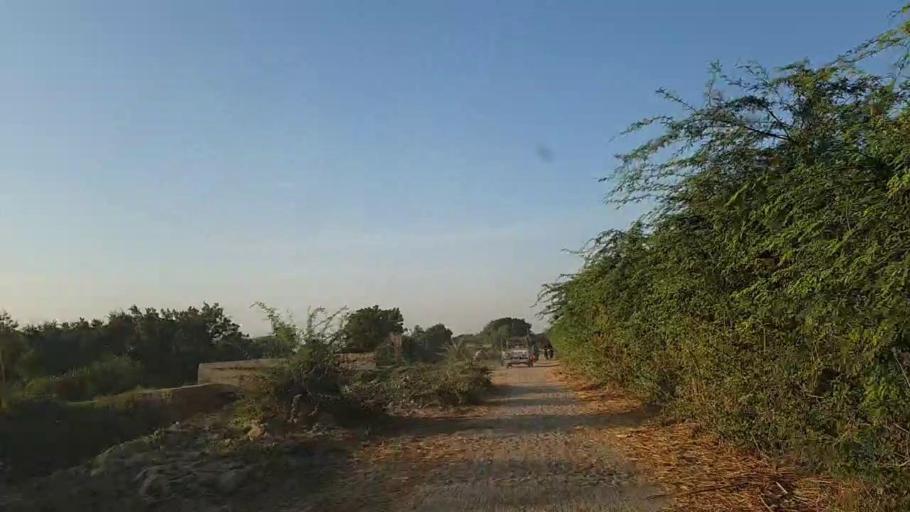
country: PK
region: Sindh
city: Mirpur Batoro
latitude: 24.7092
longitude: 68.2151
